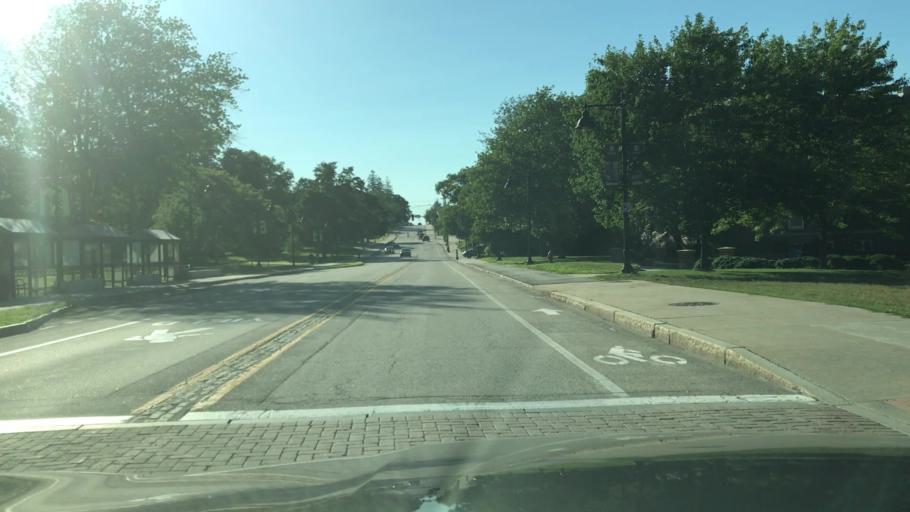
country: US
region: New Hampshire
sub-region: Strafford County
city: Durham
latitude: 43.1370
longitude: -70.9321
